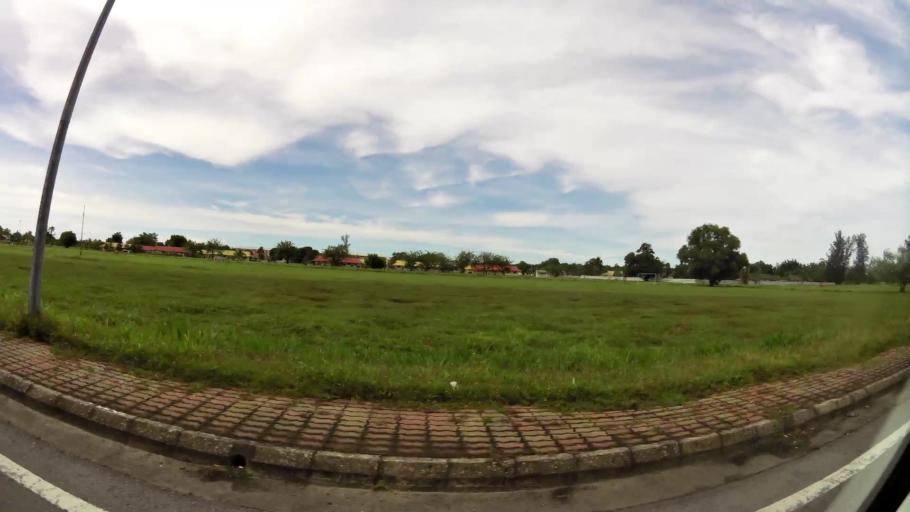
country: BN
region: Belait
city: Seria
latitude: 4.6086
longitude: 114.3086
